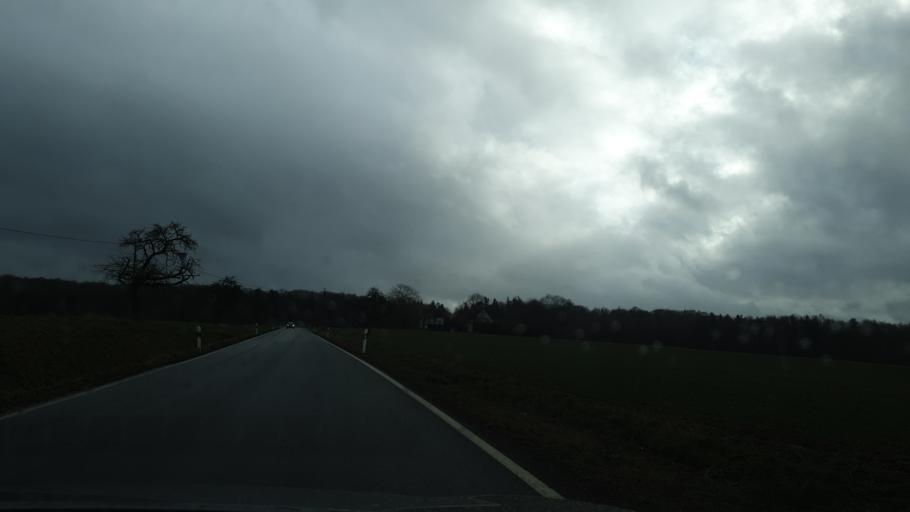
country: DE
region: Rheinland-Pfalz
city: Bettendorf
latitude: 50.2288
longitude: 7.8719
